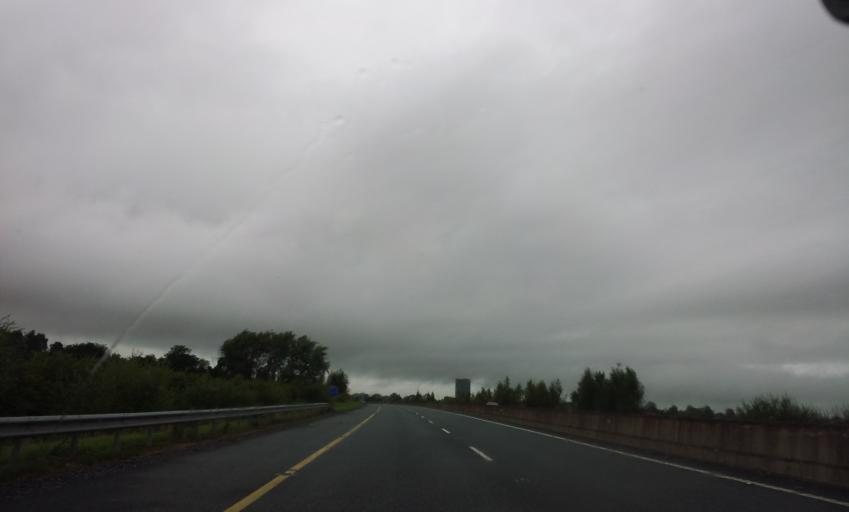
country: IE
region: Munster
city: Cahir
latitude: 52.4065
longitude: -7.9134
